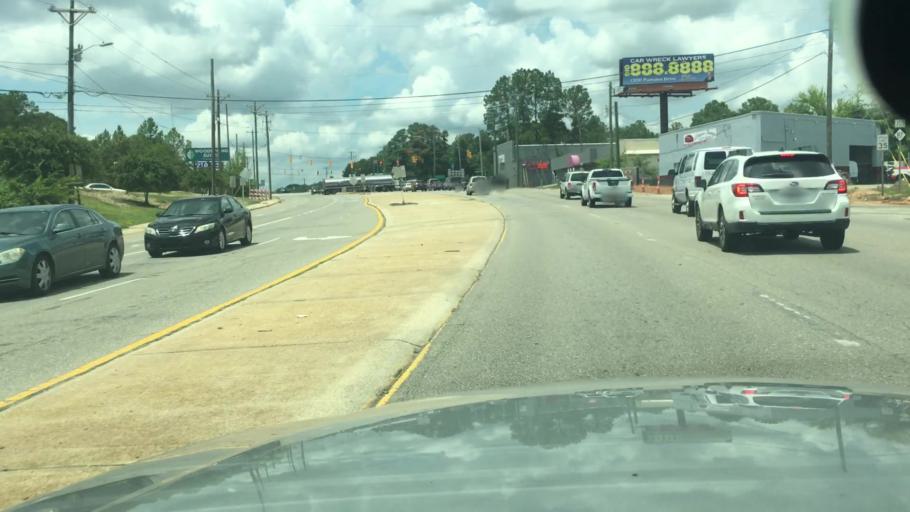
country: US
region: North Carolina
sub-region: Cumberland County
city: Fayetteville
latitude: 35.0613
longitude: -78.8887
